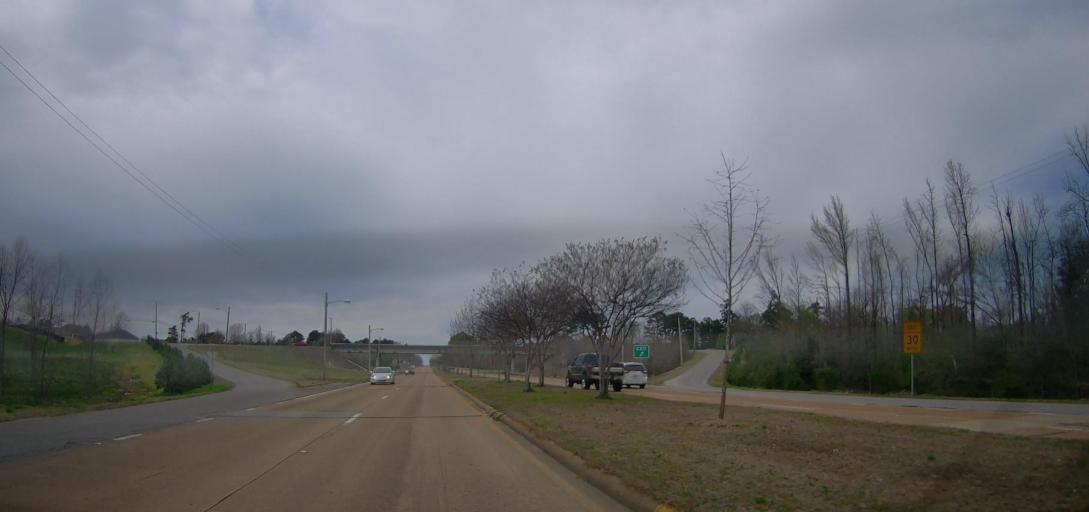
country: US
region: Mississippi
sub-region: Lee County
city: Tupelo
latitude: 34.2774
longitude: -88.7236
